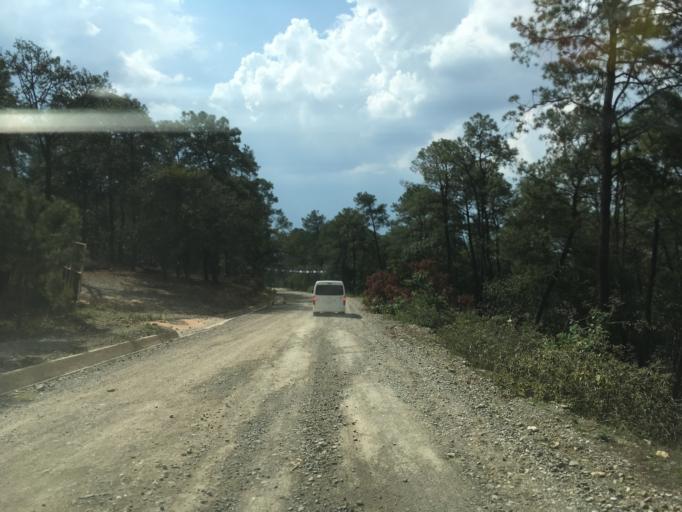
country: MX
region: Oaxaca
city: Santiago Tilantongo
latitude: 17.2090
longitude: -97.2770
